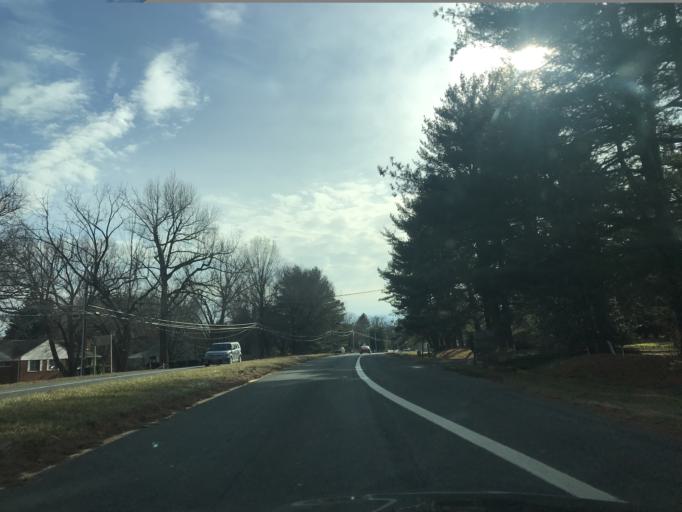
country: US
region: Maryland
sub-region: Prince George's County
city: Woodmore
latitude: 38.9423
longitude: -76.7991
